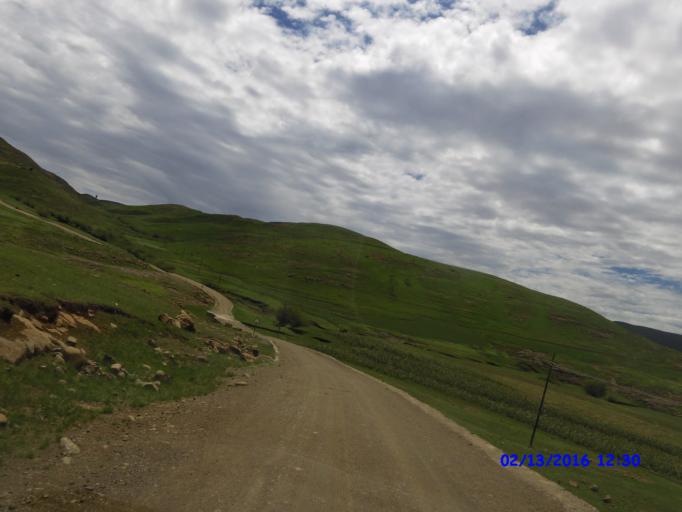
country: LS
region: Maseru
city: Nako
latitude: -29.8591
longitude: 28.0369
